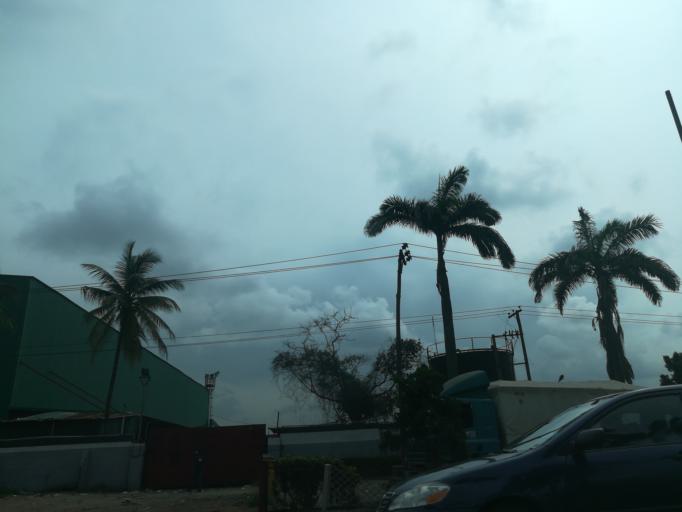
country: NG
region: Lagos
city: Ojota
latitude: 6.6024
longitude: 3.3731
